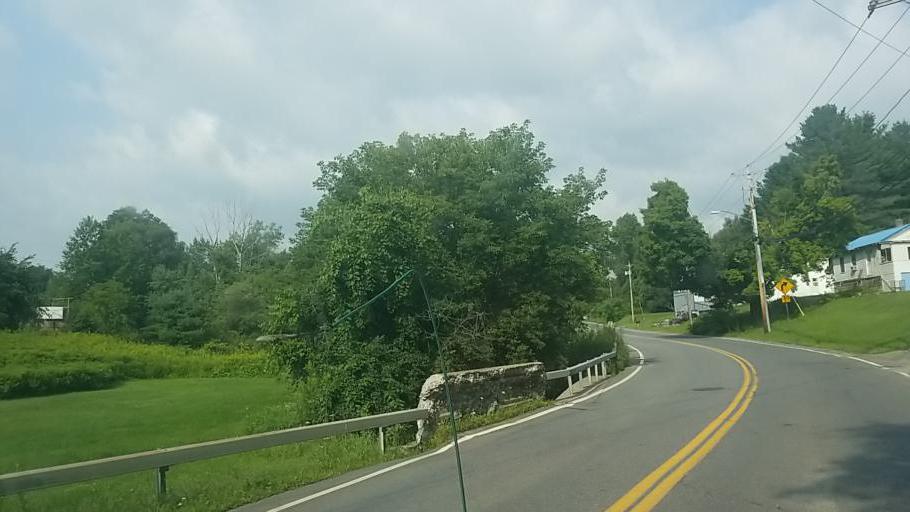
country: US
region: New York
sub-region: Fulton County
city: Gloversville
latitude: 43.0505
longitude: -74.3626
